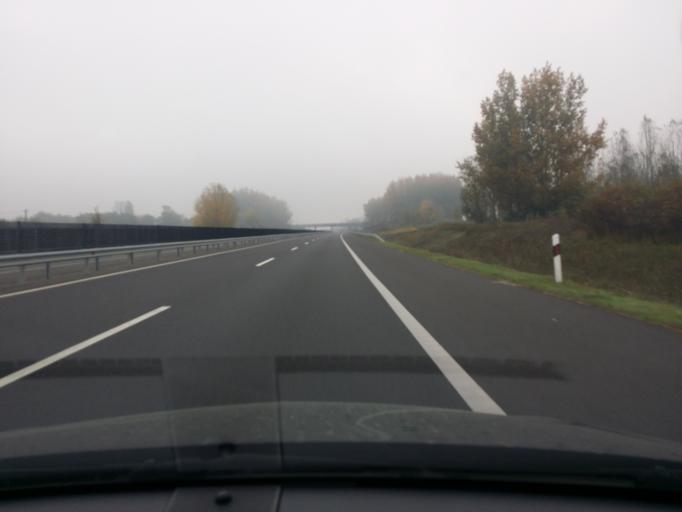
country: HU
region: Szabolcs-Szatmar-Bereg
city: Kalmanhaza
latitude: 47.9007
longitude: 21.5954
